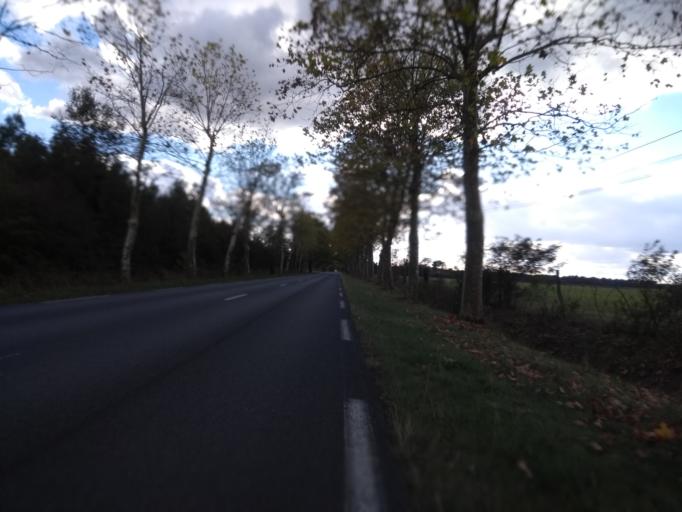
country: FR
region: Aquitaine
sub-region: Departement de la Gironde
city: Saint-Aubin-de-Medoc
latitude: 44.6914
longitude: -0.7151
